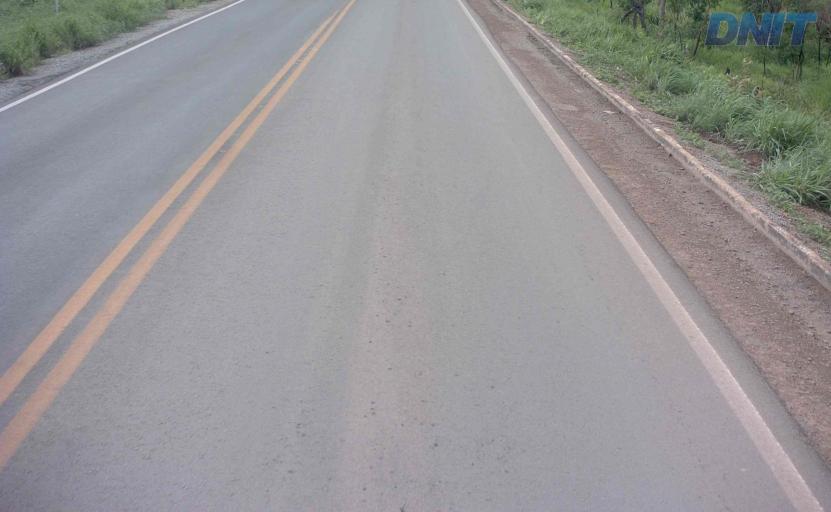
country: BR
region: Goias
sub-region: Padre Bernardo
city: Padre Bernardo
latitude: -15.1789
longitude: -48.2854
